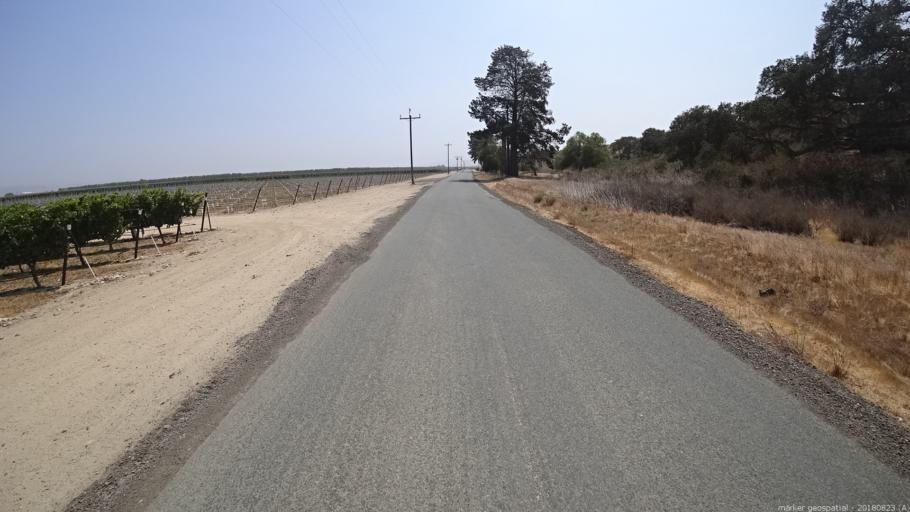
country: US
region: California
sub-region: Monterey County
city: Soledad
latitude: 36.3629
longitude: -121.3079
